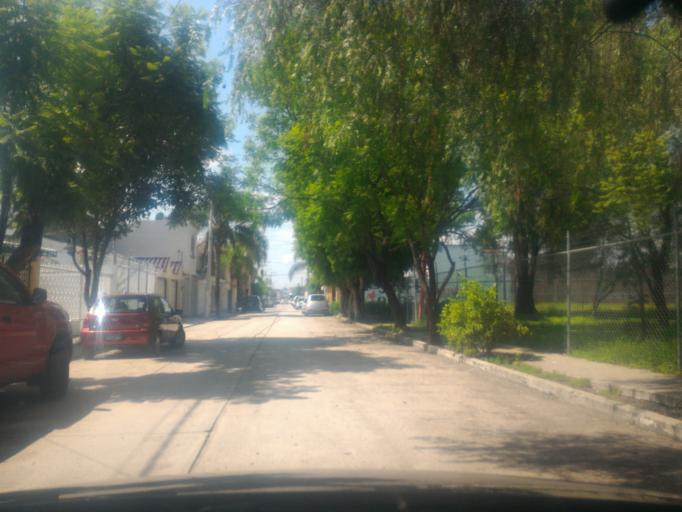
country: MX
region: Guanajuato
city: San Francisco del Rincon
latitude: 21.0112
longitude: -101.8634
